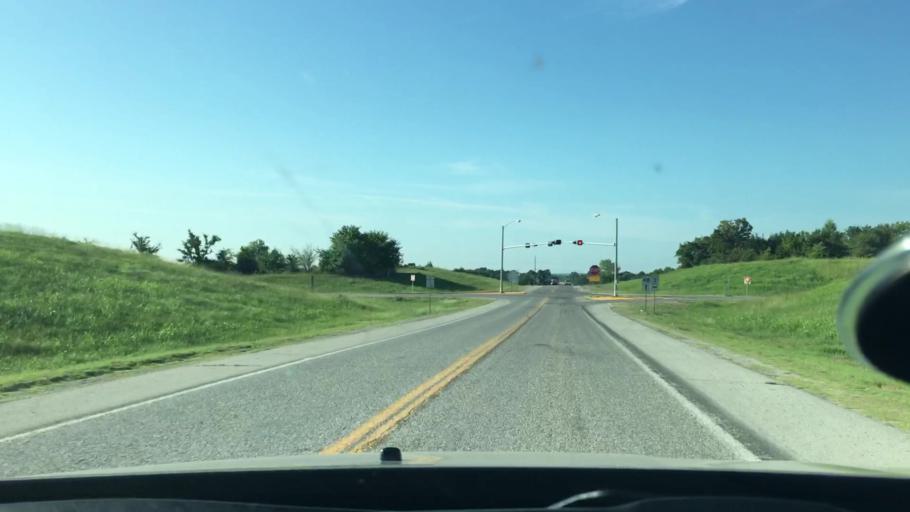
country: US
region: Oklahoma
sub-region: Coal County
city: Coalgate
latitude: 34.6121
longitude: -96.4244
